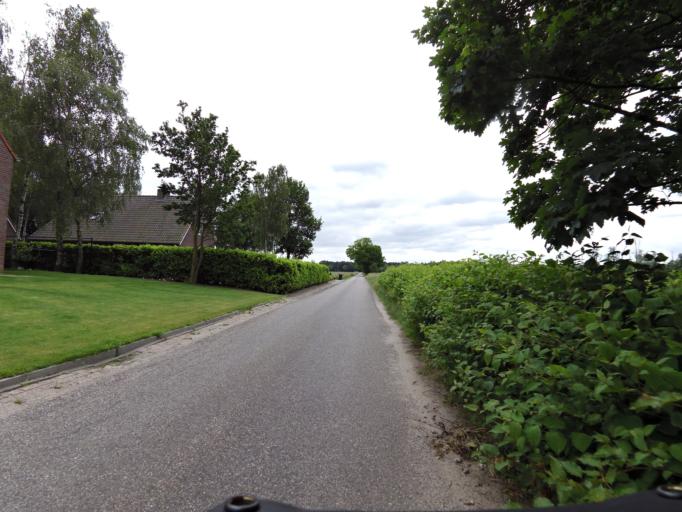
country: BE
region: Flanders
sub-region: Provincie Antwerpen
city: Baarle-Hertog
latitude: 51.4676
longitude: 4.8370
